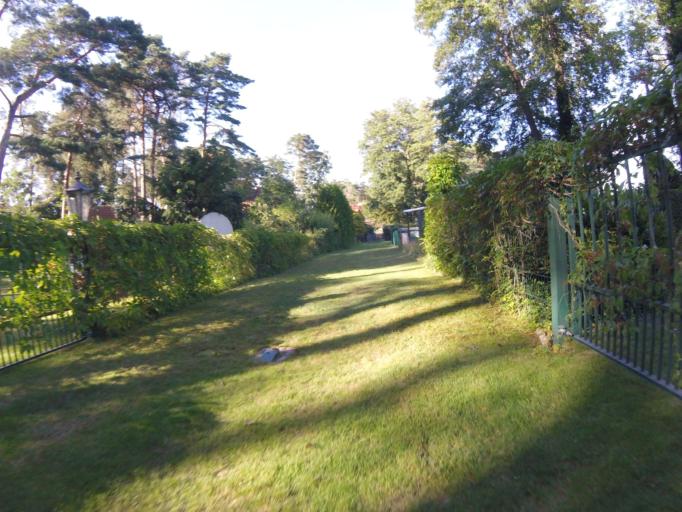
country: DE
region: Brandenburg
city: Wildau
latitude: 52.3148
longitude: 13.7059
